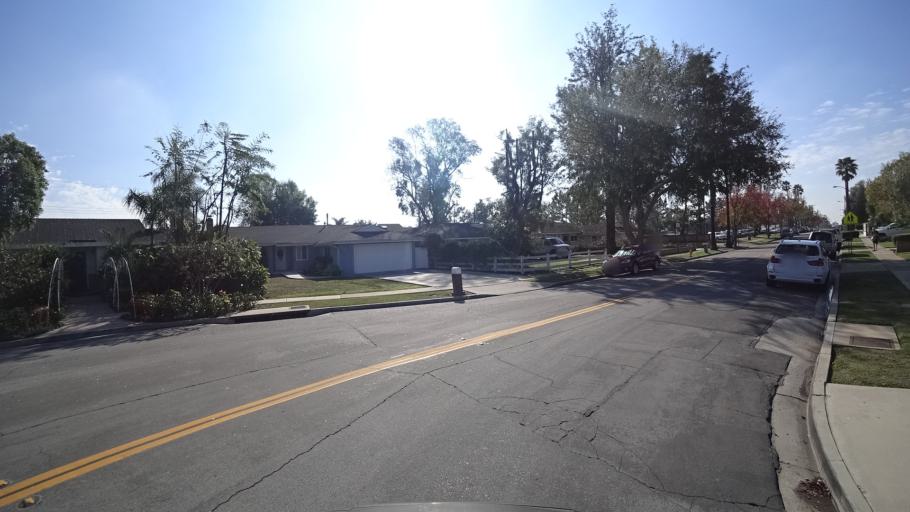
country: US
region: California
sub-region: Orange County
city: North Tustin
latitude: 33.7525
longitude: -117.8044
